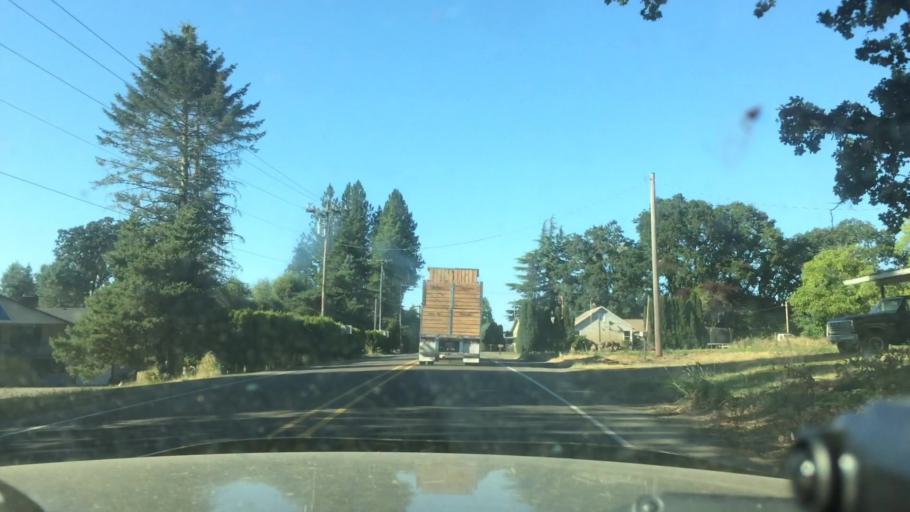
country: US
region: Oregon
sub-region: Marion County
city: Hayesville
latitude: 45.0729
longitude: -122.9788
